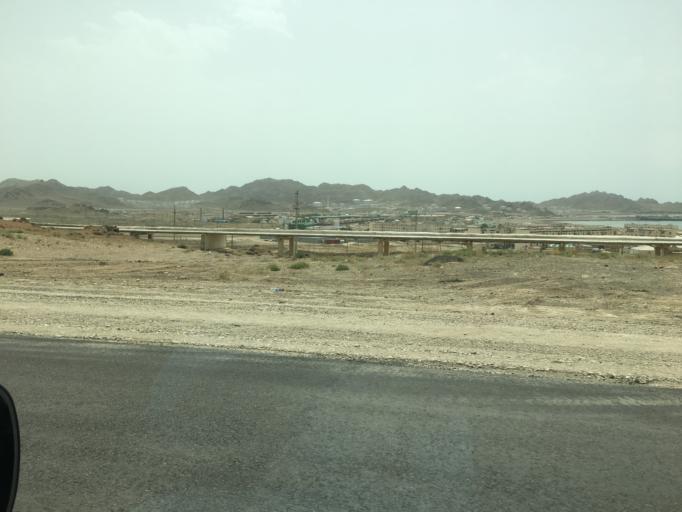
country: TM
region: Balkan
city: Turkmenbasy
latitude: 40.0133
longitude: 53.0710
